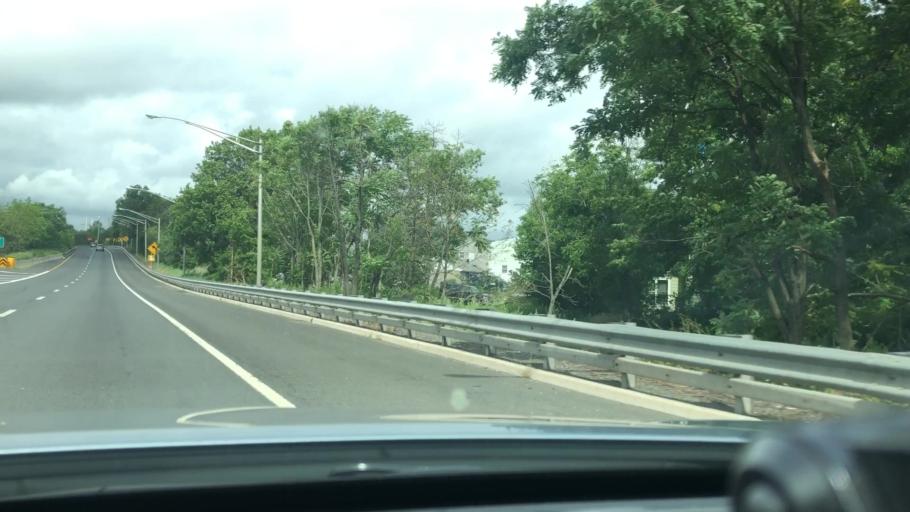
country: US
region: New Jersey
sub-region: Union County
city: Elizabeth
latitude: 40.6417
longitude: -74.2252
